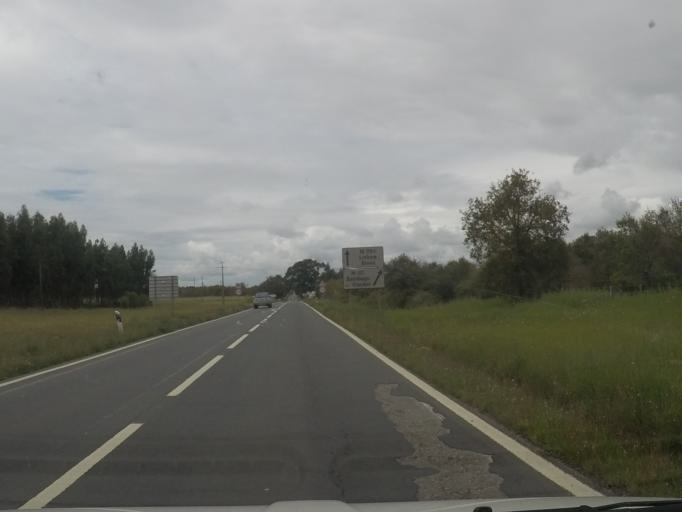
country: PT
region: Setubal
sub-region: Santiago do Cacem
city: Cercal
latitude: 37.8491
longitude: -8.7093
